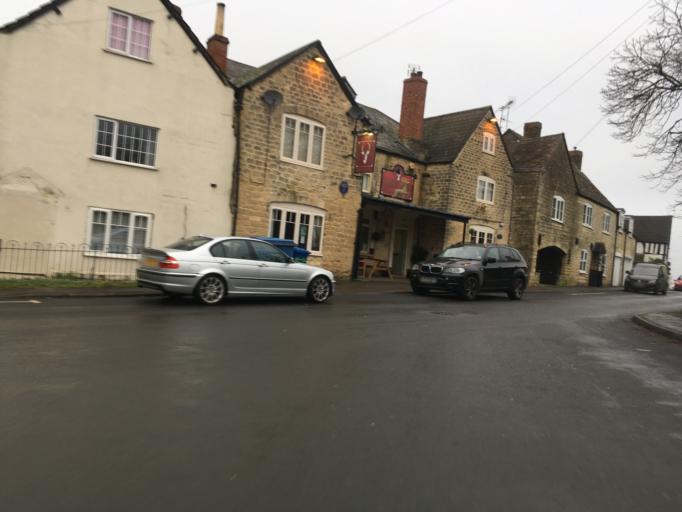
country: GB
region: England
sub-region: Gloucestershire
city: Stonehouse
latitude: 51.7284
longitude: -2.2873
